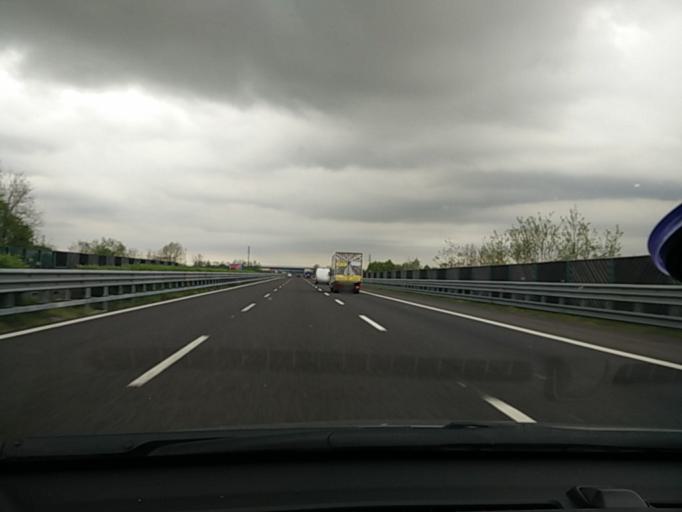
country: IT
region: Veneto
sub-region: Provincia di Treviso
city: Carbonera
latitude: 45.7050
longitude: 12.2927
